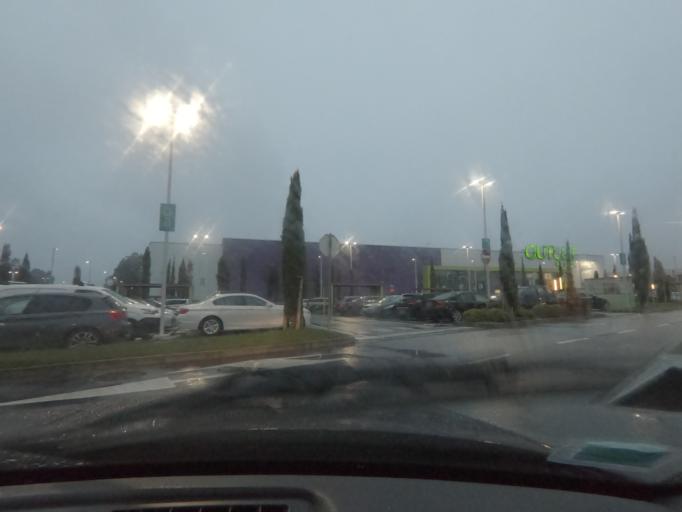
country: PT
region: Porto
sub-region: Matosinhos
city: Lavra
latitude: 41.2990
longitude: -8.7084
